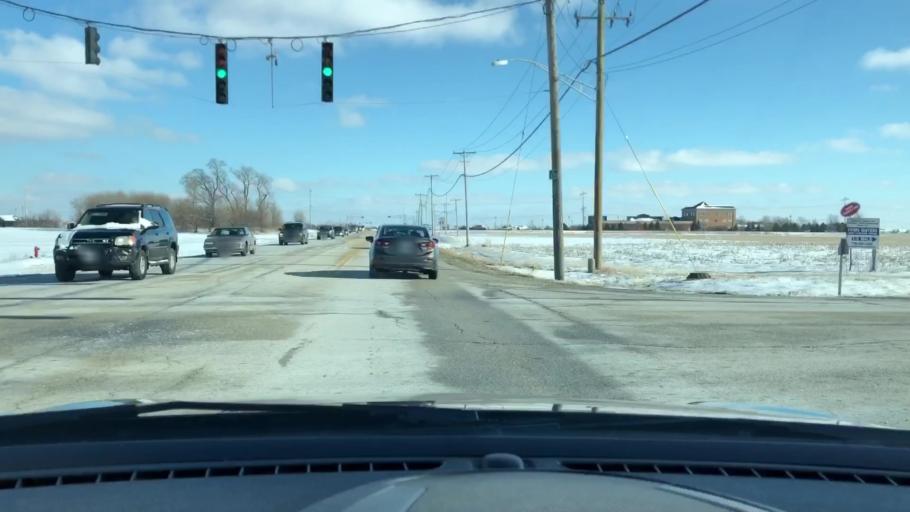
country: US
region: Illinois
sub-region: Will County
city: New Lenox
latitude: 41.4831
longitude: -87.9647
